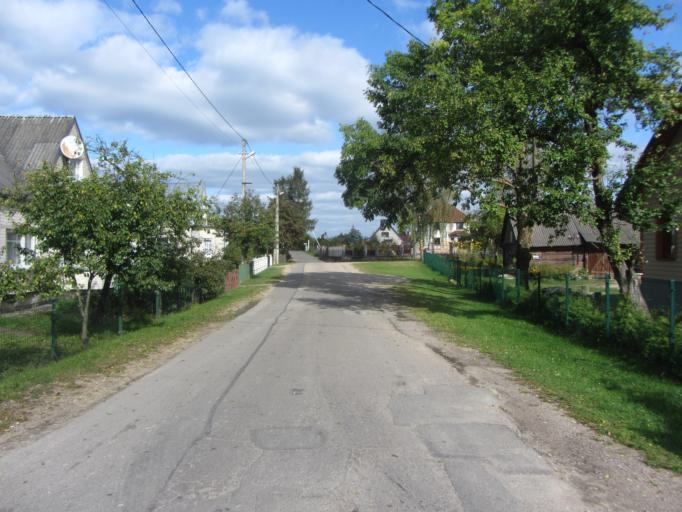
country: LT
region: Vilnius County
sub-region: Trakai
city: Rudiskes
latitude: 54.5183
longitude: 24.8241
